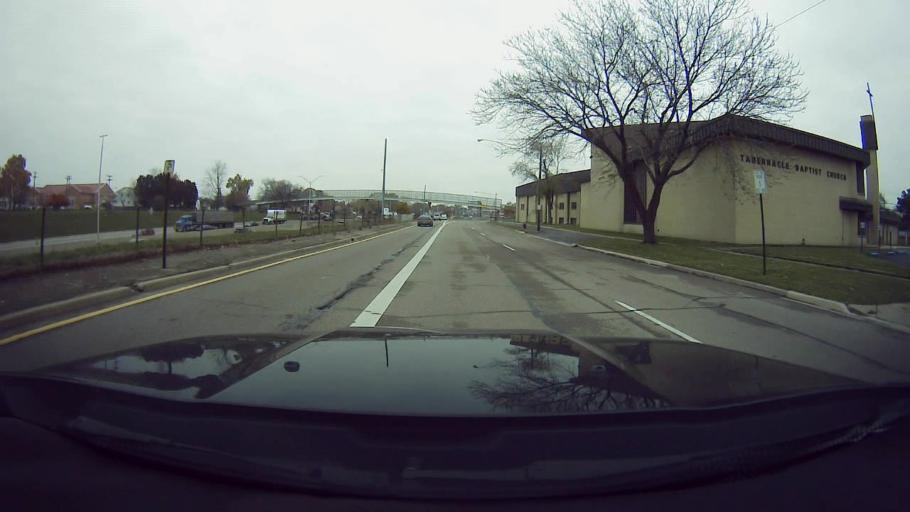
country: US
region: Michigan
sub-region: Oakland County
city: Hazel Park
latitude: 42.4583
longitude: -83.1020
